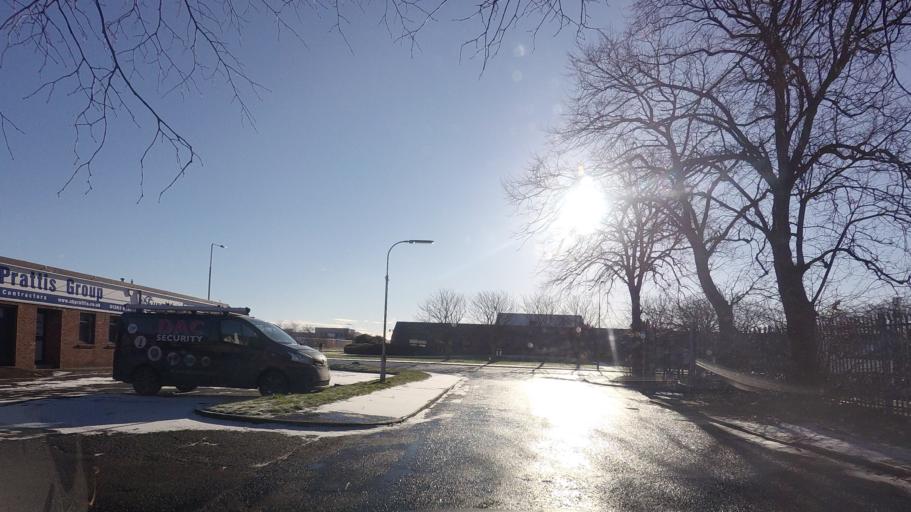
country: GB
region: Scotland
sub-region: Fife
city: Crossgates
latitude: 56.0431
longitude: -3.3548
